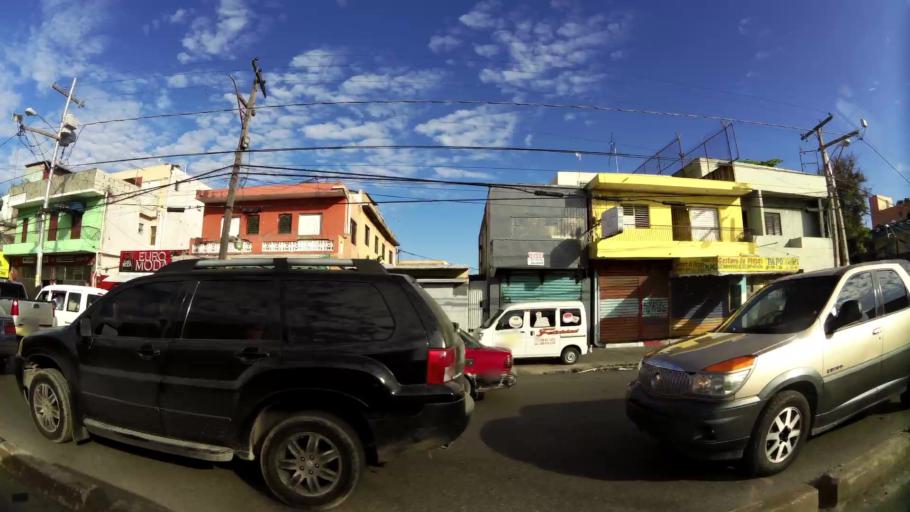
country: DO
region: Nacional
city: Ensanche Luperon
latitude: 18.4994
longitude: -69.8903
